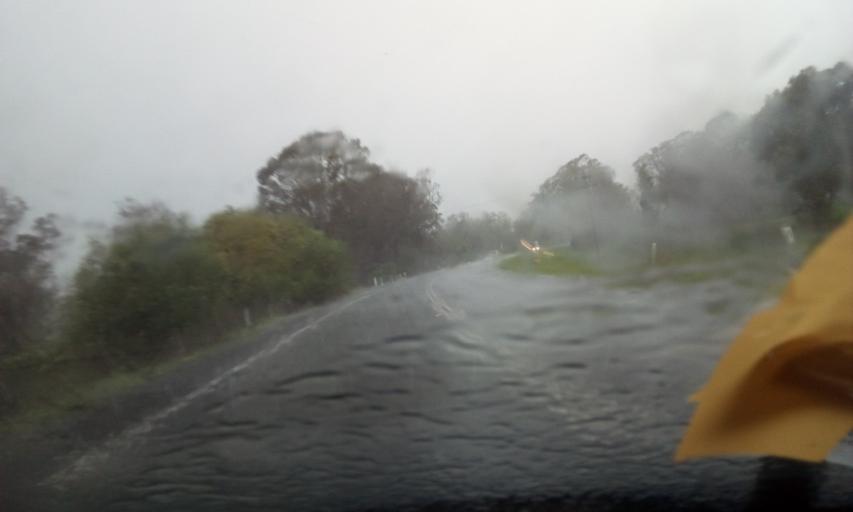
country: AU
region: New South Wales
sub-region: Camden
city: Camden South
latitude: -34.1041
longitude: 150.6980
